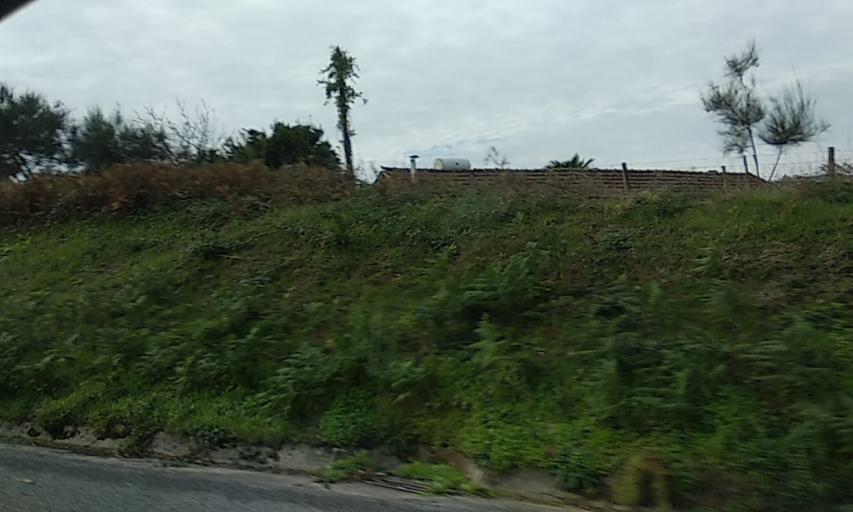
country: PT
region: Porto
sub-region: Santo Tirso
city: Santo Tirso
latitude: 41.3637
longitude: -8.5002
